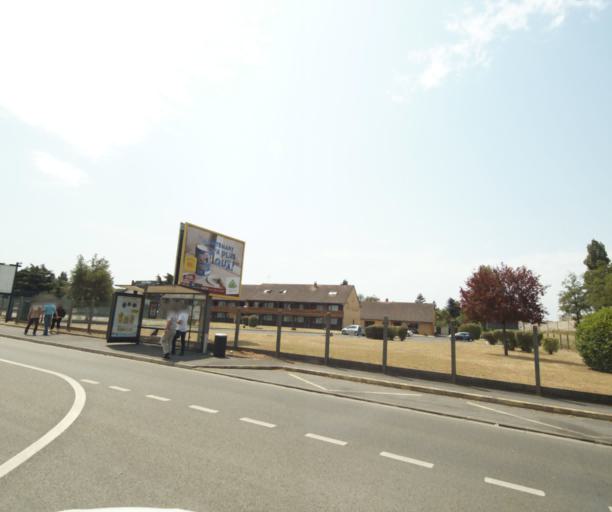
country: FR
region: Ile-de-France
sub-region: Departement des Yvelines
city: Conflans-Sainte-Honorine
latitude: 49.0061
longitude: 2.0851
